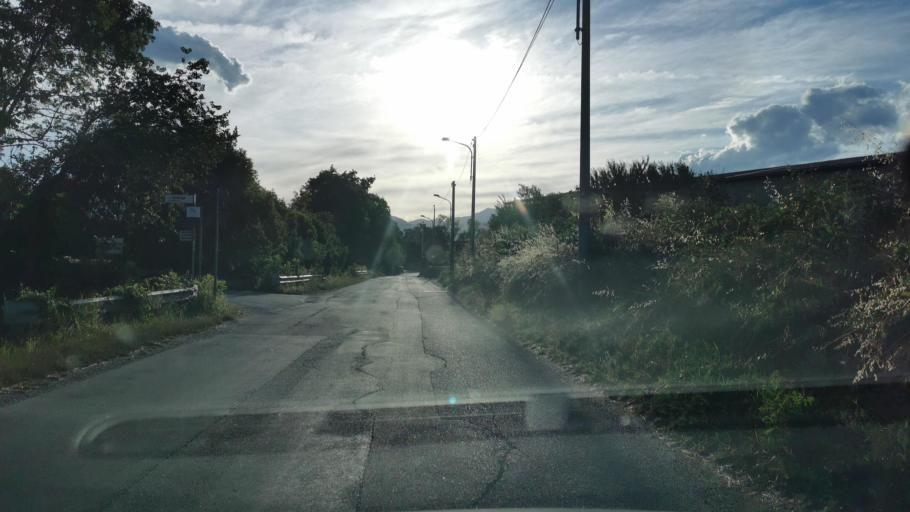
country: IT
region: Piedmont
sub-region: Provincia di Torino
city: Pianezza
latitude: 45.1234
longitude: 7.5511
